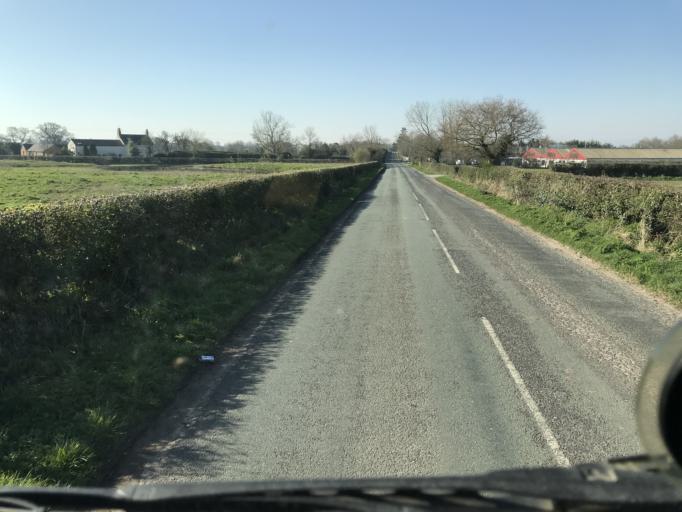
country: GB
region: England
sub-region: Cheshire West and Chester
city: Waverton
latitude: 53.1683
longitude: -2.8219
